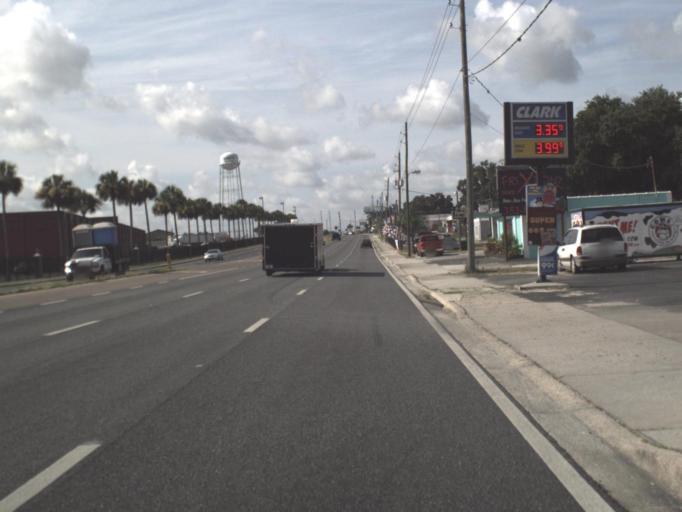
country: US
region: Florida
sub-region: Pasco County
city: Dade City North
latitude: 28.3819
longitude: -82.1930
